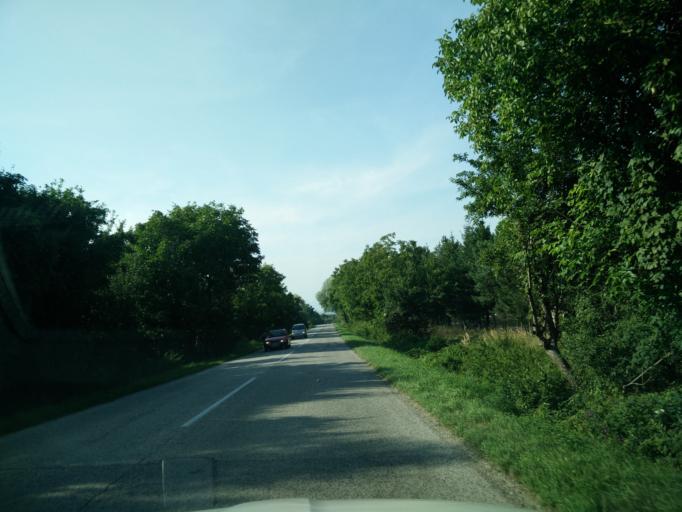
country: SK
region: Nitriansky
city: Novaky
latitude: 48.7012
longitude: 18.5931
